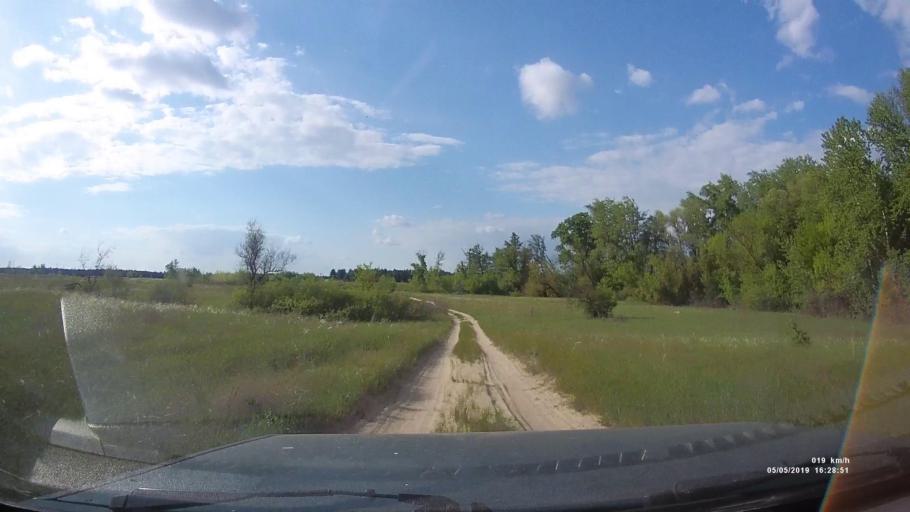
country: RU
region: Rostov
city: Ust'-Donetskiy
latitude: 47.7688
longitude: 41.0153
